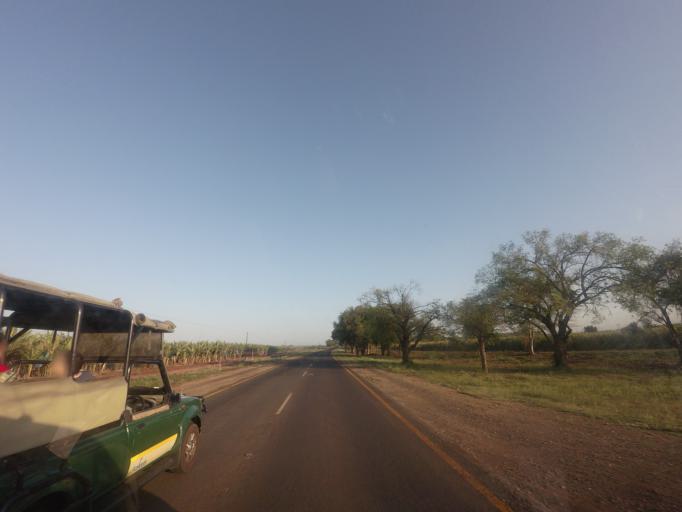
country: ZA
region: Mpumalanga
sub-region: Ehlanzeni District
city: Komatipoort
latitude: -25.3887
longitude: 31.9129
